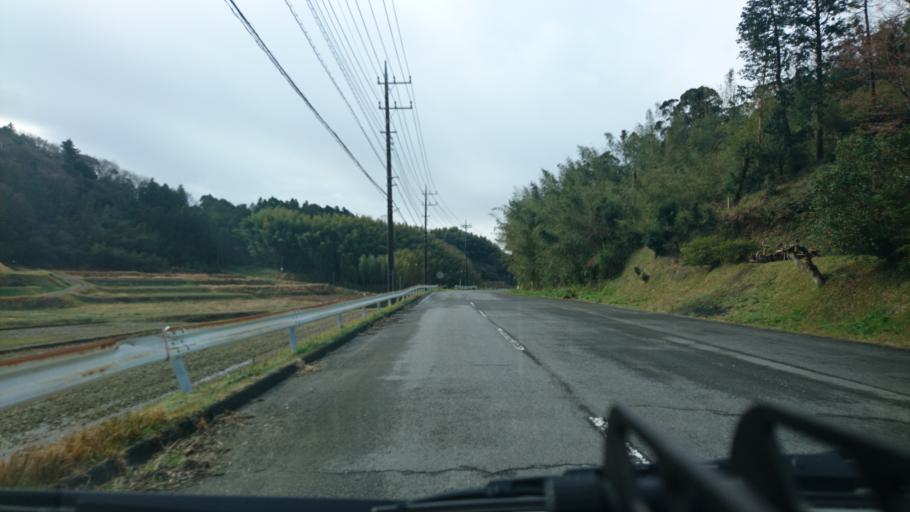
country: JP
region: Chiba
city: Kisarazu
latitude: 35.3167
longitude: 139.9640
